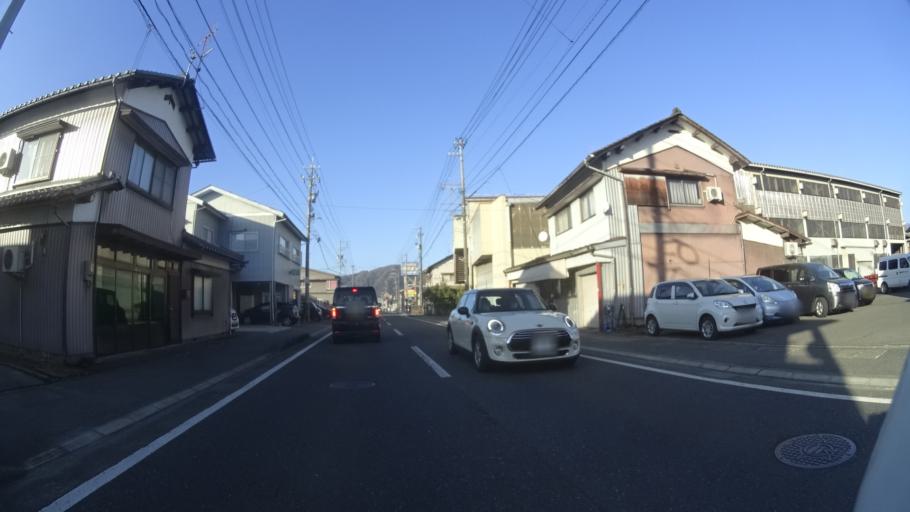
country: JP
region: Fukui
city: Ono
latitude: 35.9893
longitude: 136.4997
